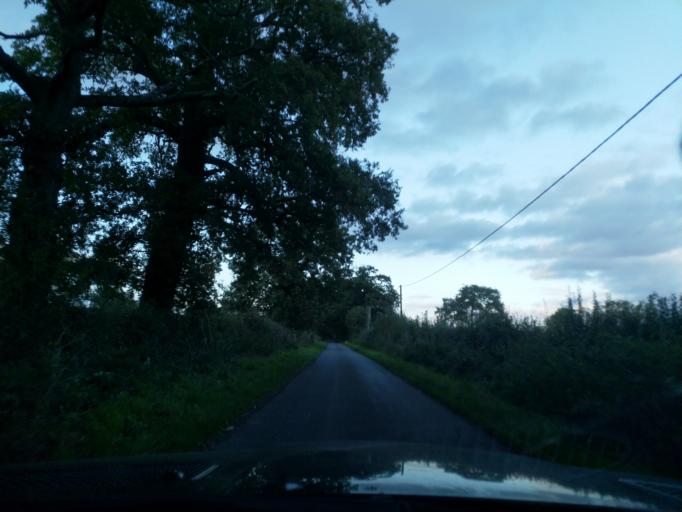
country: GB
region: England
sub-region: Warwickshire
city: Wroxall
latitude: 52.3398
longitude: -1.6696
